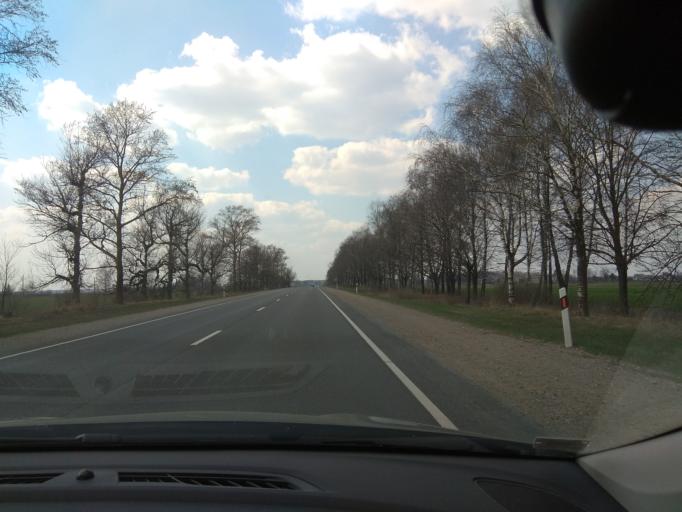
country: LT
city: Seduva
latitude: 55.7666
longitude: 23.7245
